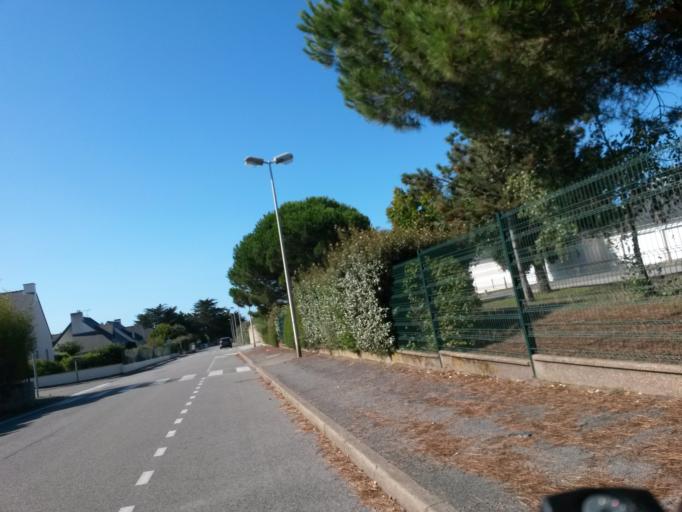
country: FR
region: Pays de la Loire
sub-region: Departement de la Loire-Atlantique
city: Guerande
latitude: 47.3221
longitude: -2.4316
